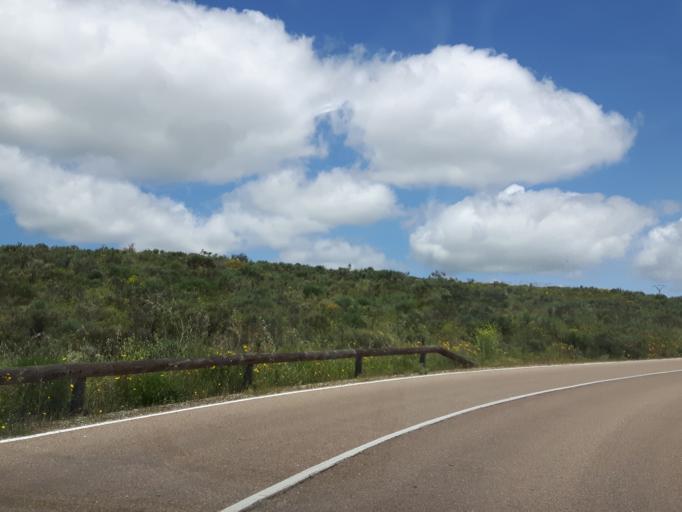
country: ES
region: Castille and Leon
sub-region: Provincia de Salamanca
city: Castillejo de Martin Viejo
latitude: 40.6981
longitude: -6.6619
